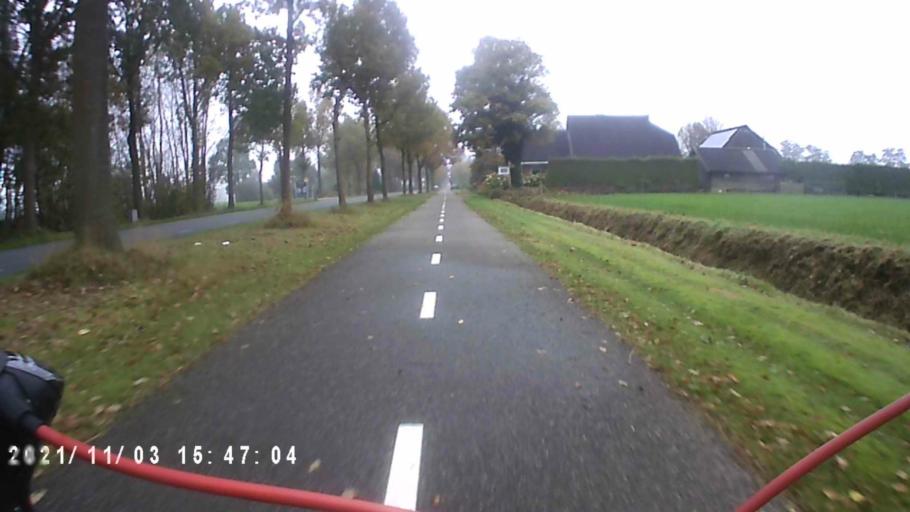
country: NL
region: Groningen
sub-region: Gemeente Leek
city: Leek
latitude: 53.0918
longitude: 6.3403
